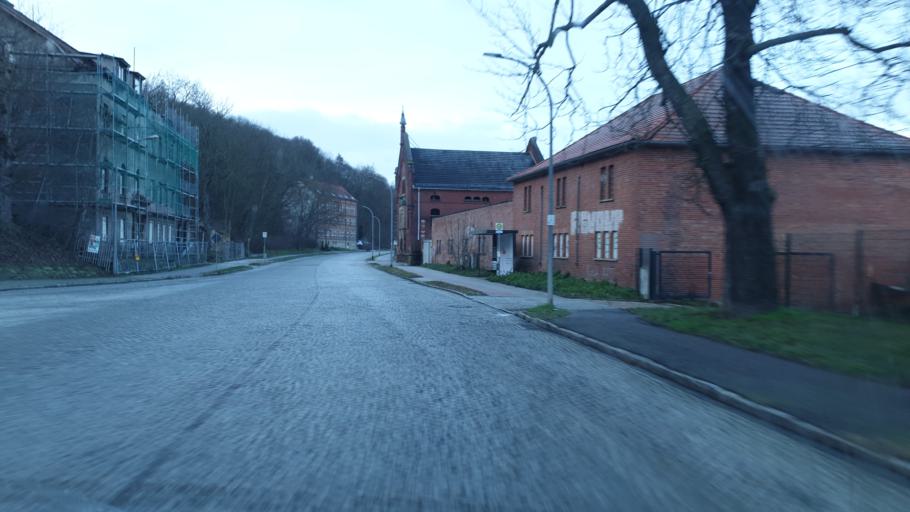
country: DE
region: Saxony-Anhalt
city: Burgwerben
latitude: 51.2089
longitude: 11.9831
